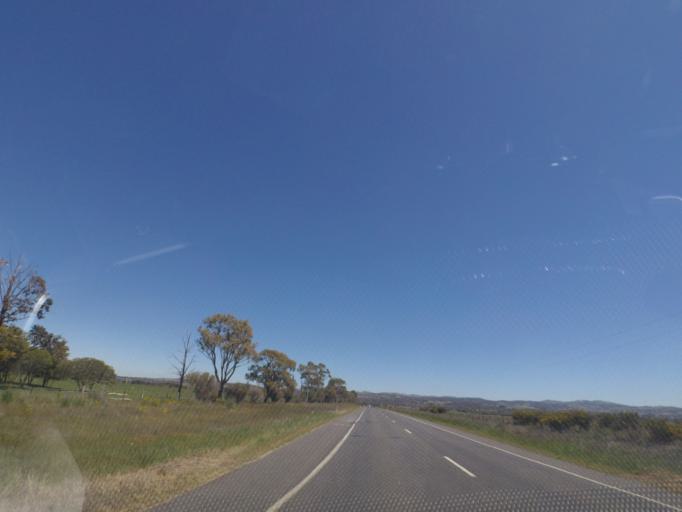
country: AU
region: Victoria
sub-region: Whittlesea
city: Whittlesea
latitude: -37.2899
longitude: 144.8968
